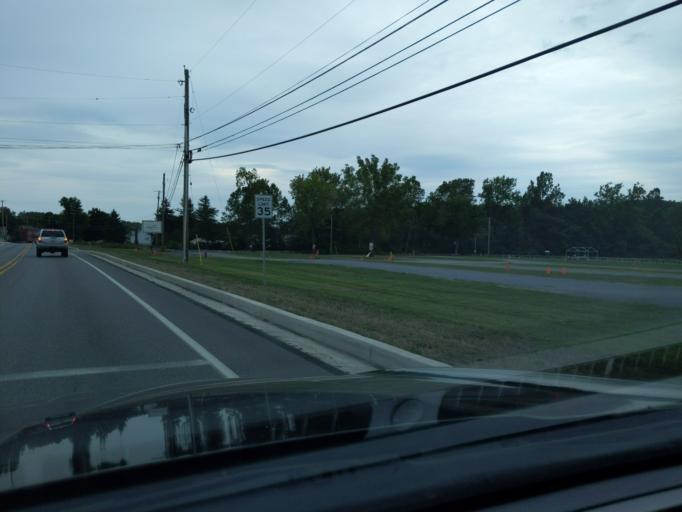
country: US
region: Pennsylvania
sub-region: Blair County
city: Duncansville
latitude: 40.3887
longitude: -78.4347
